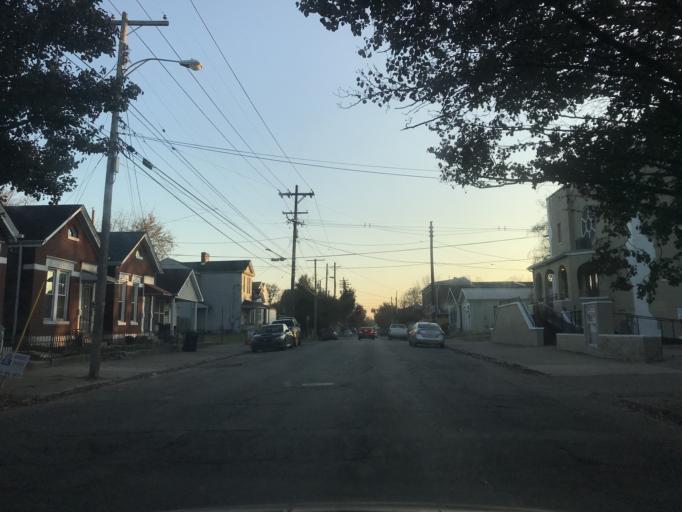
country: US
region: Kentucky
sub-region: Jefferson County
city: Louisville
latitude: 38.2510
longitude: -85.7343
